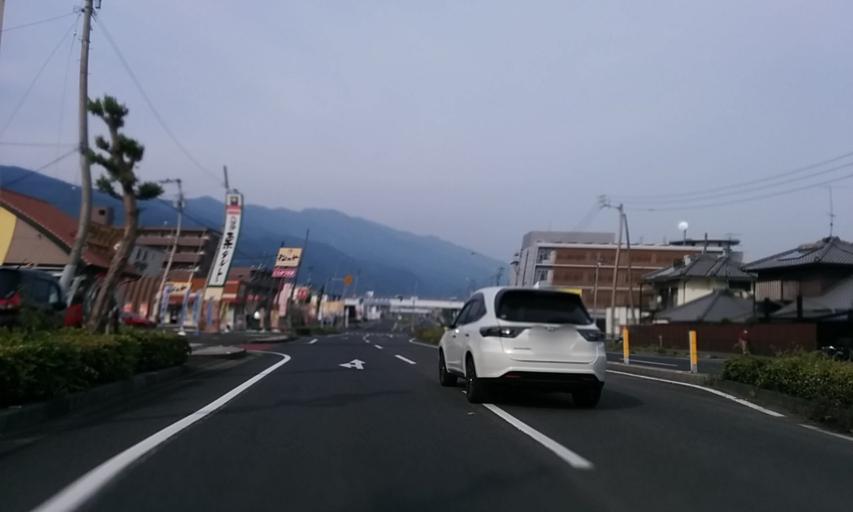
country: JP
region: Ehime
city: Kawanoecho
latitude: 33.9795
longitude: 133.5520
